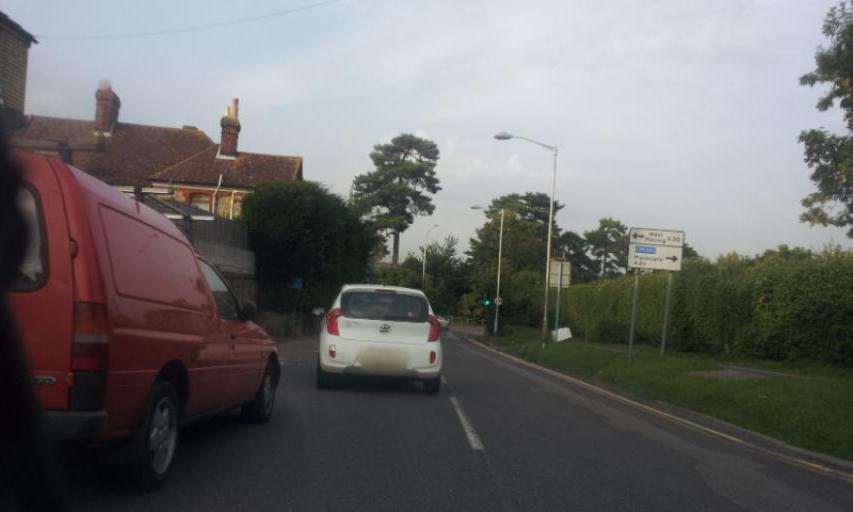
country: GB
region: England
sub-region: Kent
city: Aylesford
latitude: 51.2982
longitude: 0.4547
